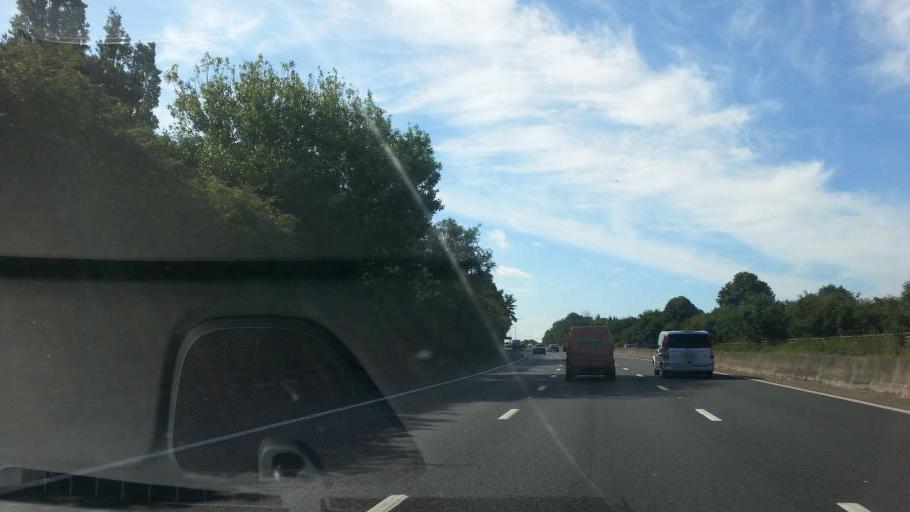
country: GB
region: England
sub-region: Hertfordshire
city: Welwyn Garden City
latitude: 51.7880
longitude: -0.2261
